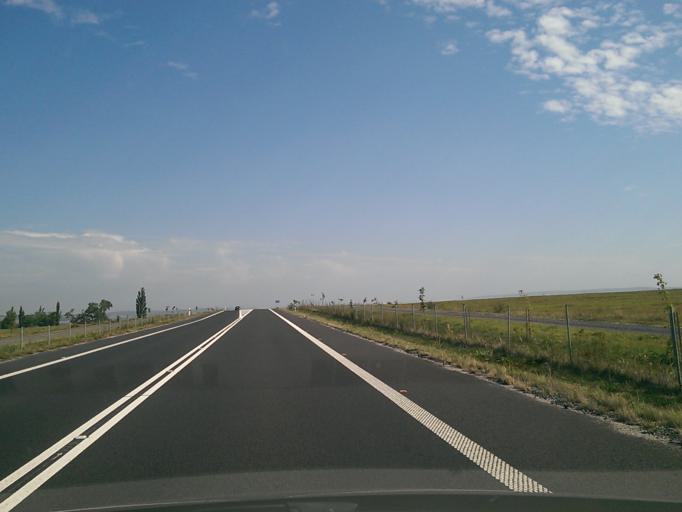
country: CZ
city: Hradek nad Nisou
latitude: 50.8841
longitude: 14.8471
